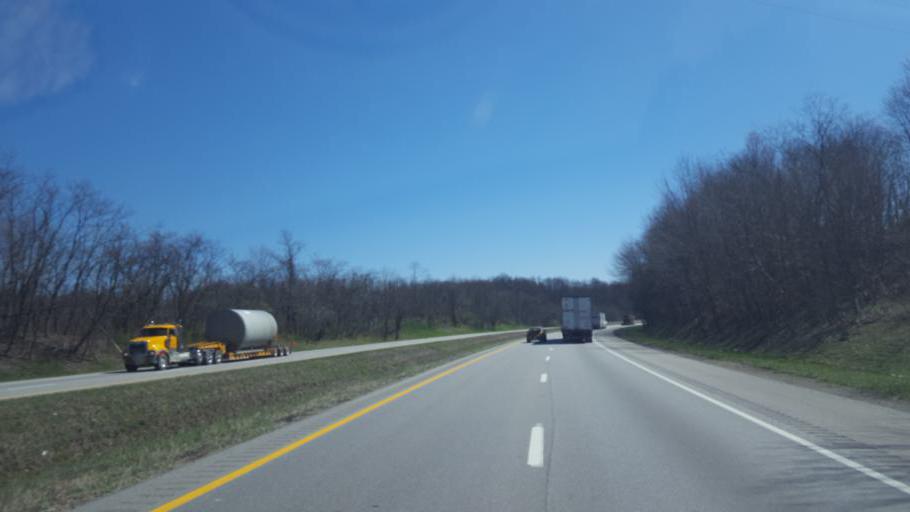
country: US
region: Ohio
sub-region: Belmont County
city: Barnesville
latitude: 40.0571
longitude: -81.2607
